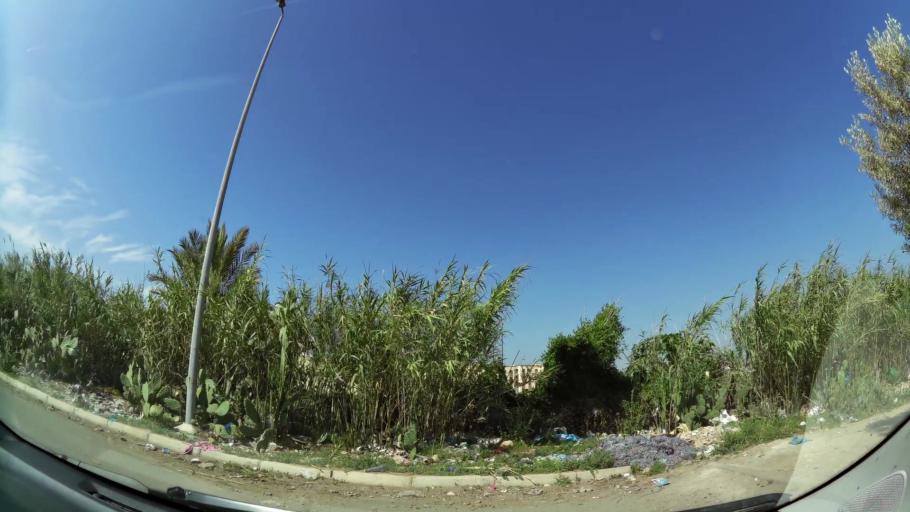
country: MA
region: Oriental
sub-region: Oujda-Angad
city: Oujda
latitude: 34.6969
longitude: -1.8751
